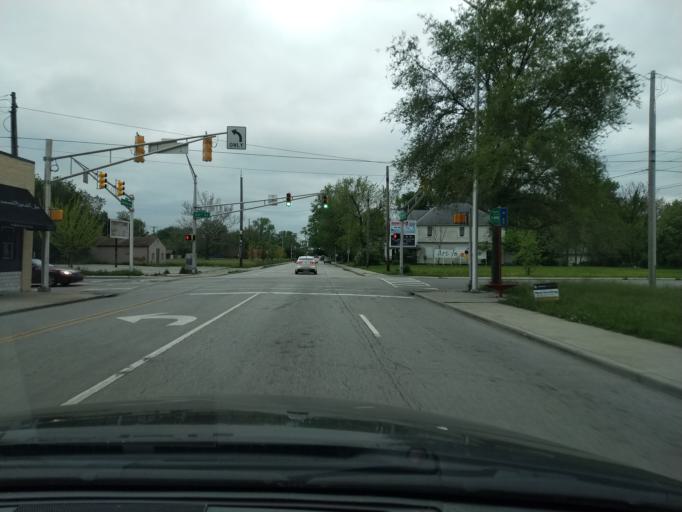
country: US
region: Indiana
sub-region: Marion County
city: Indianapolis
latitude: 39.8106
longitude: -86.1497
